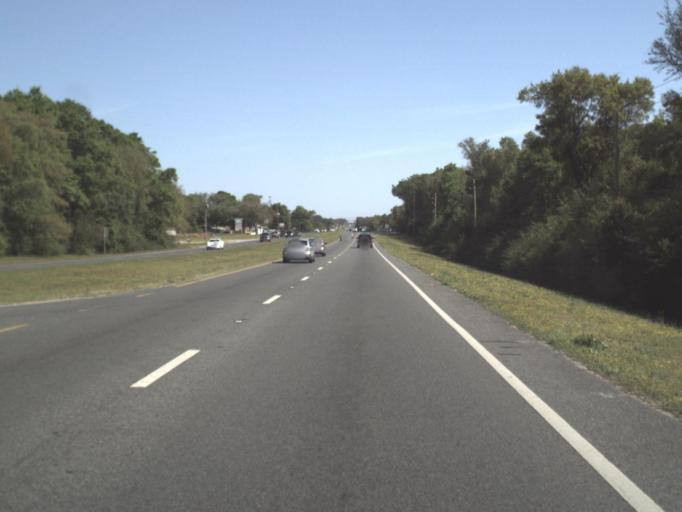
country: US
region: Florida
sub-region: Escambia County
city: Bellview
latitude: 30.4546
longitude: -87.2970
